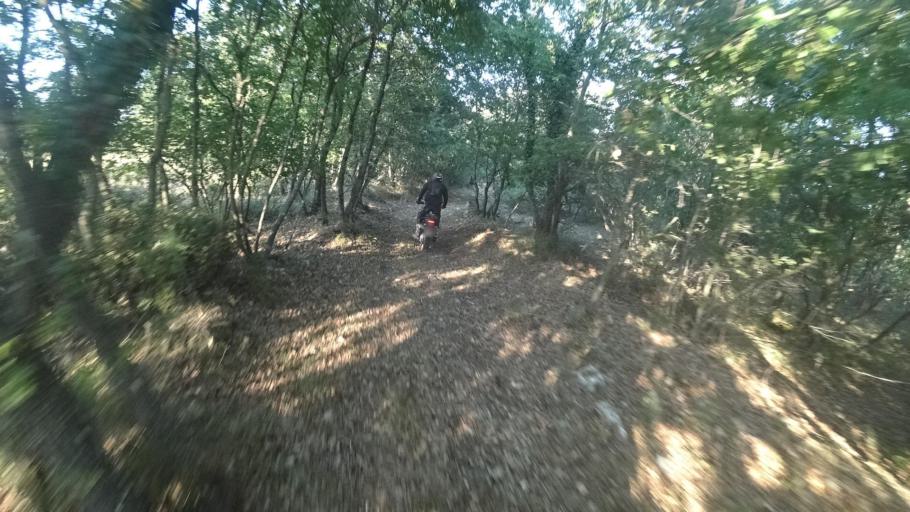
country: HR
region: Istarska
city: Marcana
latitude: 44.9602
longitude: 13.9184
